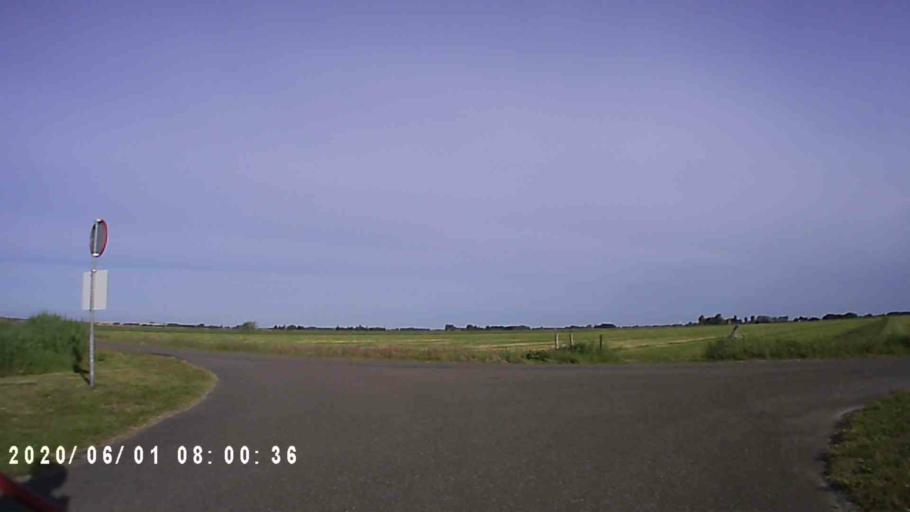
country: NL
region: Friesland
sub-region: Gemeente Dantumadiel
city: Rinsumageast
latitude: 53.2825
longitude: 5.9343
